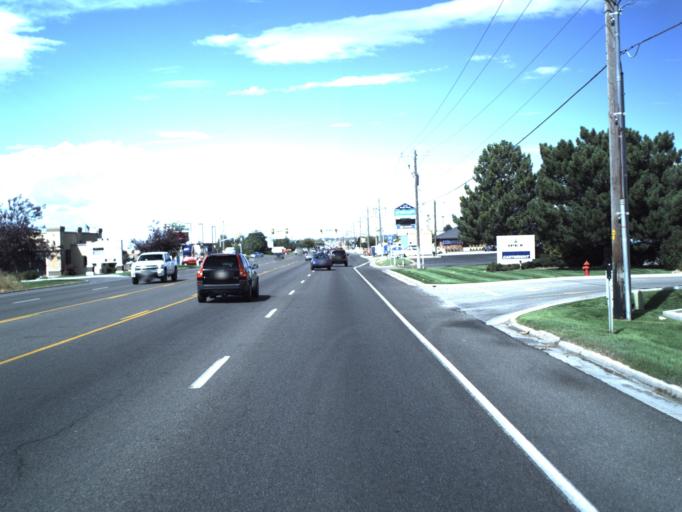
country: US
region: Utah
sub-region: Cache County
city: North Logan
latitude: 41.7703
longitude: -111.8340
